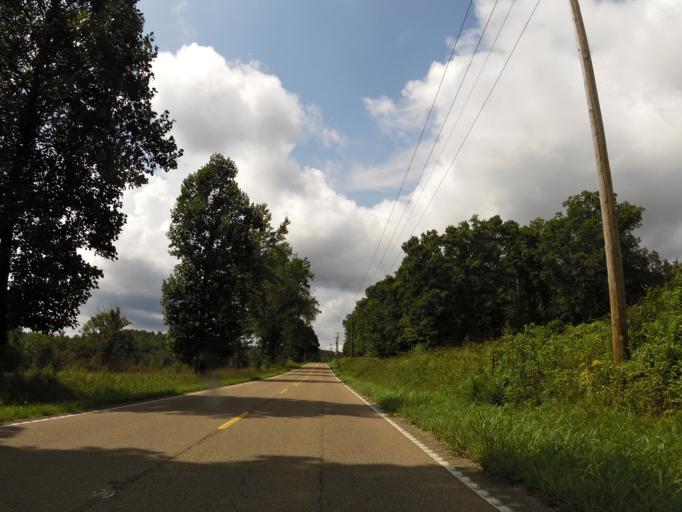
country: US
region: Tennessee
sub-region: Perry County
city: Linden
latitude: 35.6189
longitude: -87.8829
